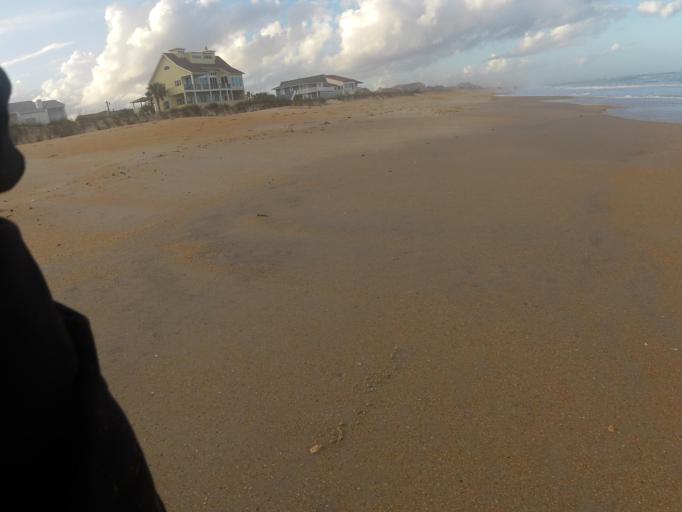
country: US
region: Florida
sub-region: Flagler County
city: Palm Coast
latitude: 29.6280
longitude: -81.1952
